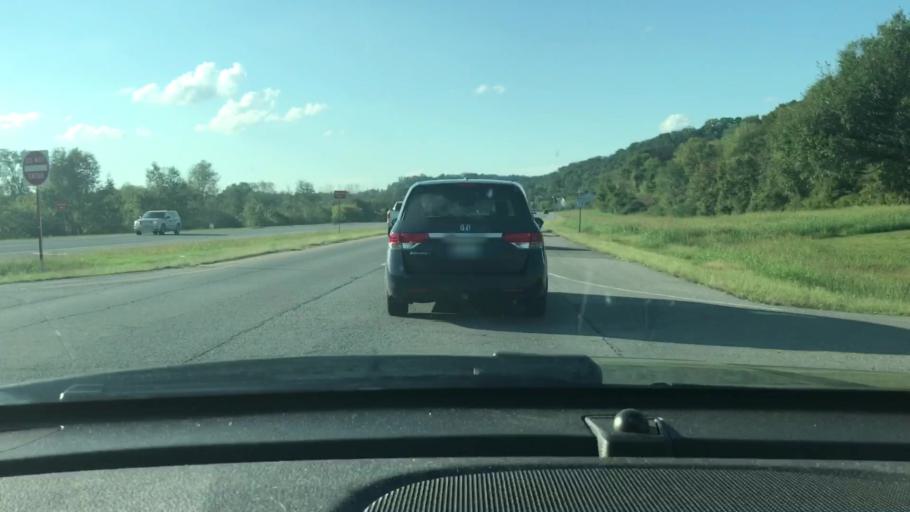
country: US
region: Tennessee
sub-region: Cheatham County
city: Ashland City
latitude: 36.2520
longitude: -87.0351
